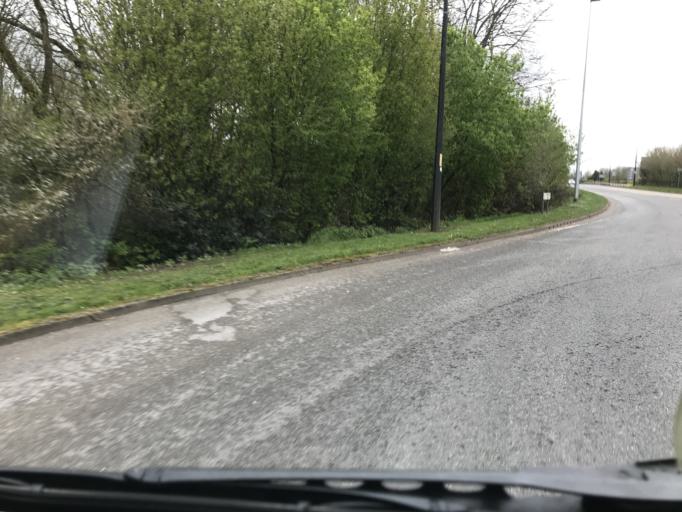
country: GB
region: England
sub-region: Trafford
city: Partington
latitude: 53.4177
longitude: -2.4469
